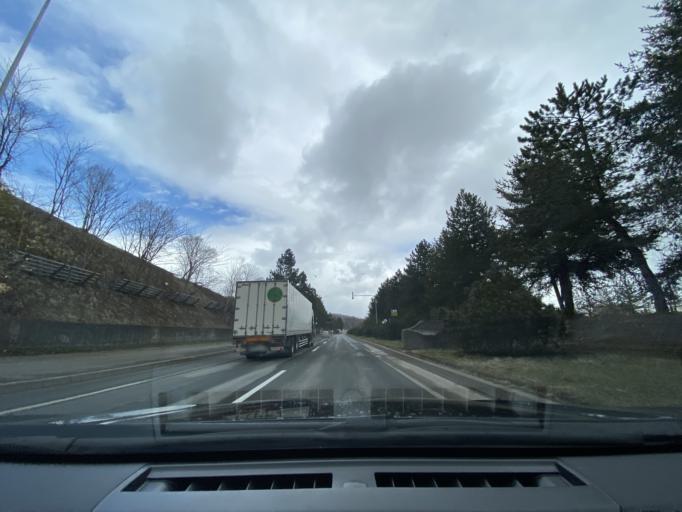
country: JP
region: Hokkaido
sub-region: Asahikawa-shi
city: Asahikawa
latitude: 43.7752
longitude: 142.3065
